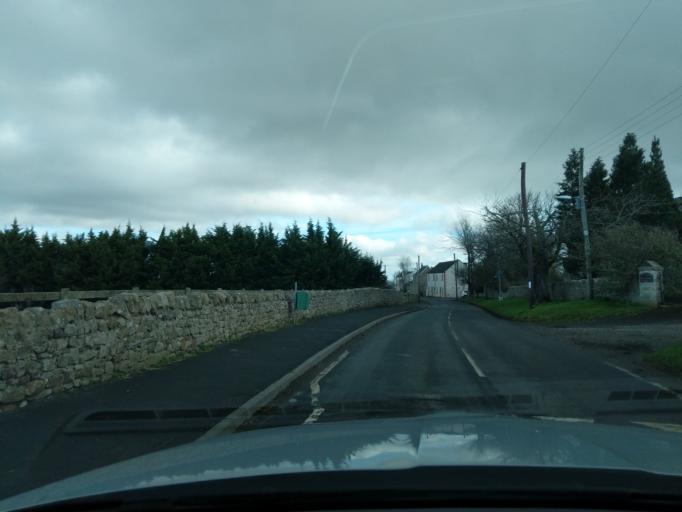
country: GB
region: England
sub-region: North Yorkshire
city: Catterick
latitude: 54.3574
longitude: -1.6694
